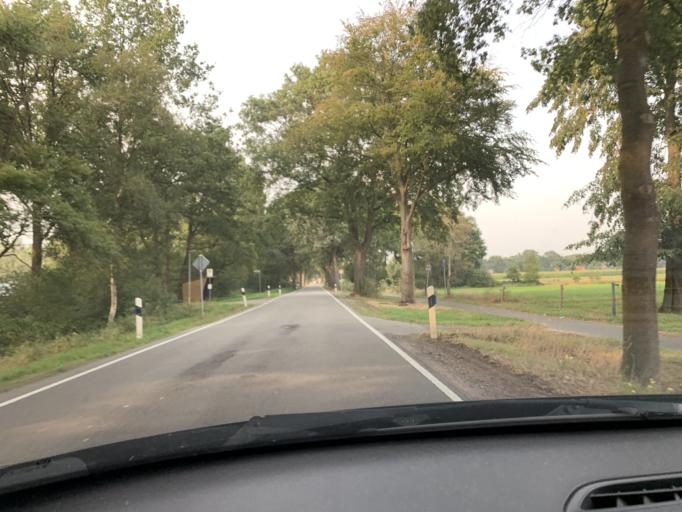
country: DE
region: Lower Saxony
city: Apen
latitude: 53.2065
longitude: 7.7945
